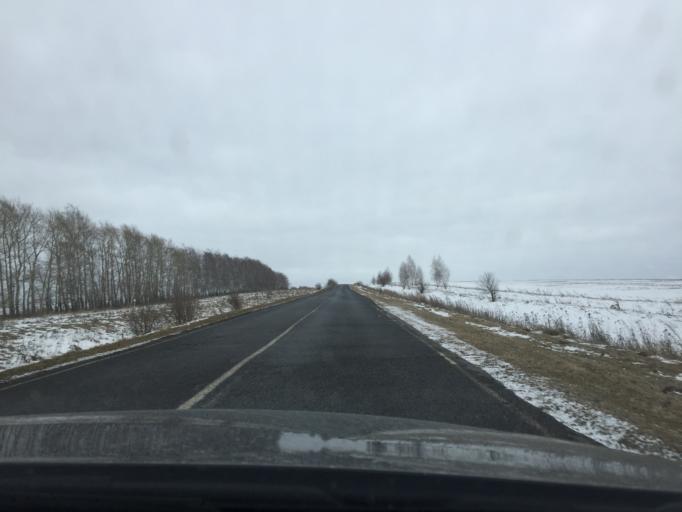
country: RU
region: Tula
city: Shchekino
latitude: 53.8285
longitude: 37.5133
